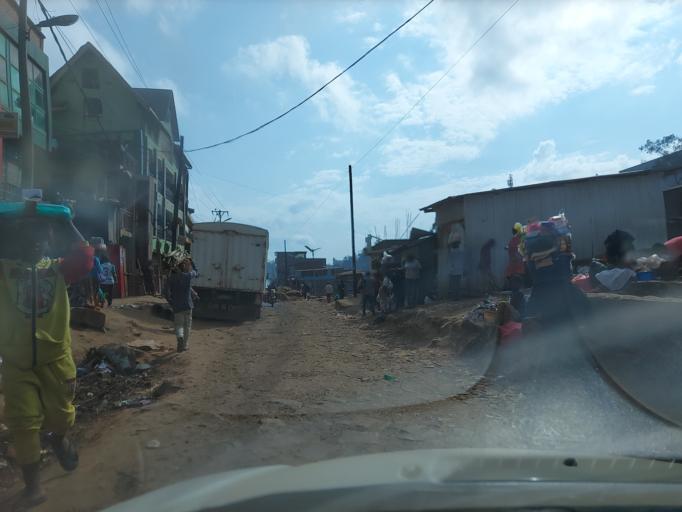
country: CD
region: South Kivu
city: Bukavu
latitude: -2.5232
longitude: 28.8525
